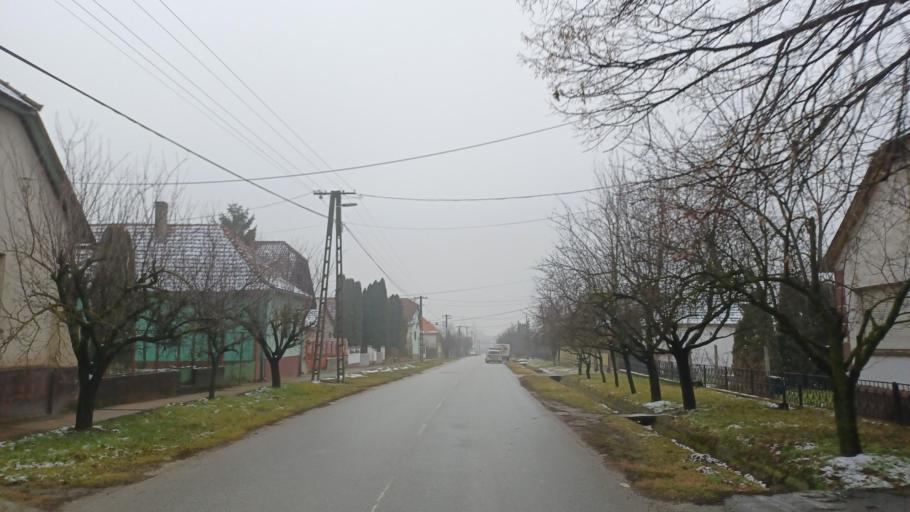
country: HU
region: Tolna
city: Gyonk
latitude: 46.5627
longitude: 18.4771
